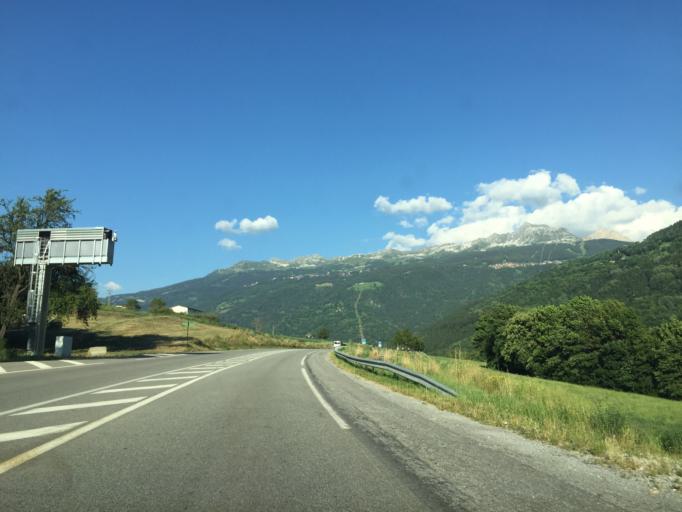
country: FR
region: Rhone-Alpes
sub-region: Departement de la Savoie
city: Macot-la-Plagne
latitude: 45.5680
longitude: 6.7039
